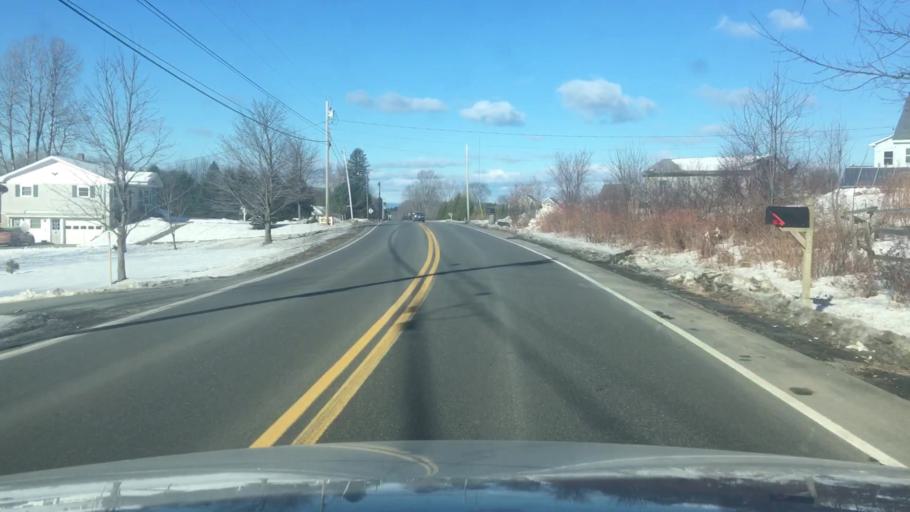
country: US
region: Maine
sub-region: Somerset County
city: Skowhegan
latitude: 44.7372
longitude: -69.6839
